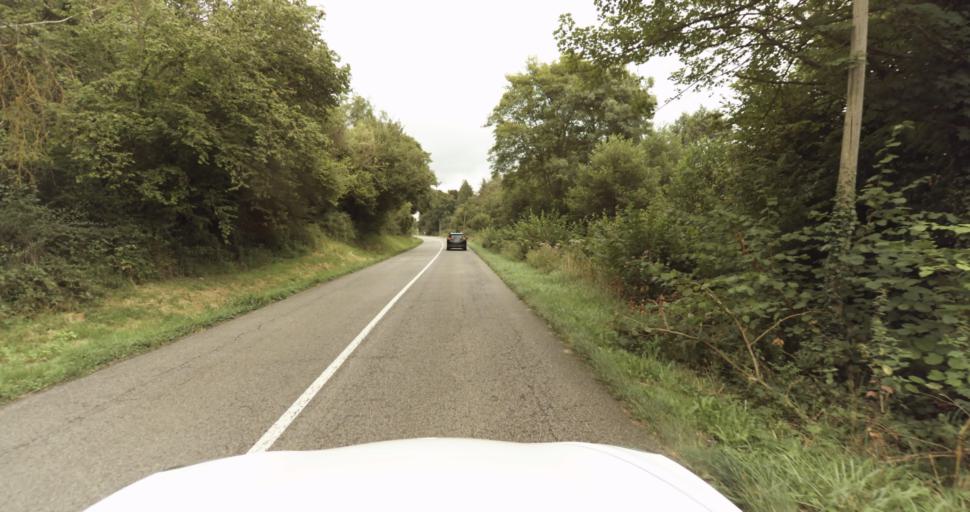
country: FR
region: Haute-Normandie
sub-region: Departement de l'Eure
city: Saint-Sebastien-de-Morsent
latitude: 48.9986
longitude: 1.0638
